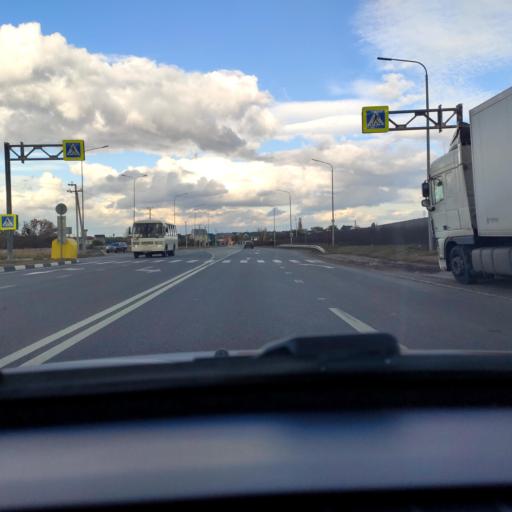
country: RU
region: Voronezj
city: Ramon'
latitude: 51.8251
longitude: 39.2512
